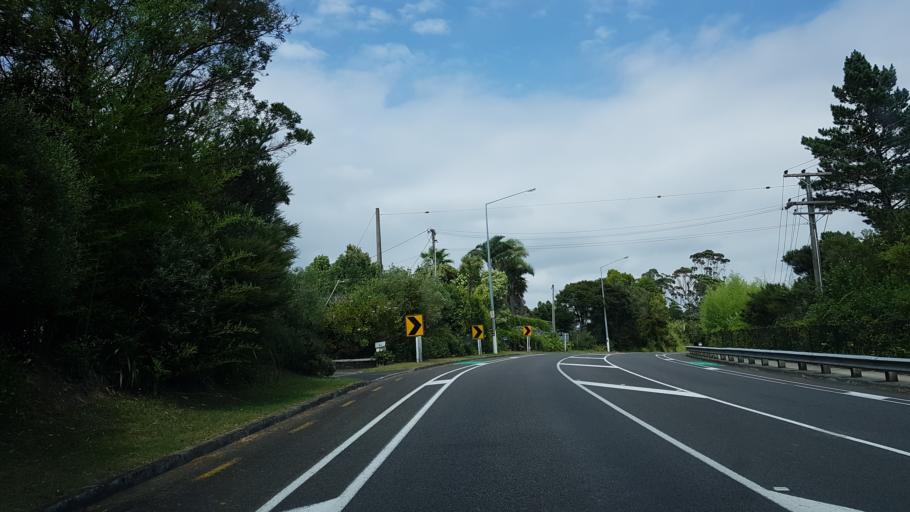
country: NZ
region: Auckland
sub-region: Auckland
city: North Shore
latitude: -36.7796
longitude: 174.6825
